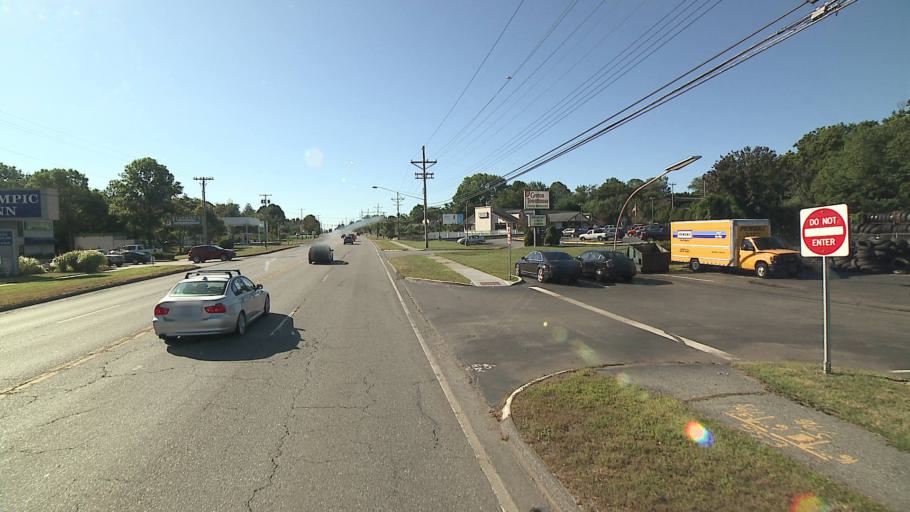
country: US
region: Connecticut
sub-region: New London County
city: Conning Towers-Nautilus Park
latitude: 41.3723
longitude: -72.0725
